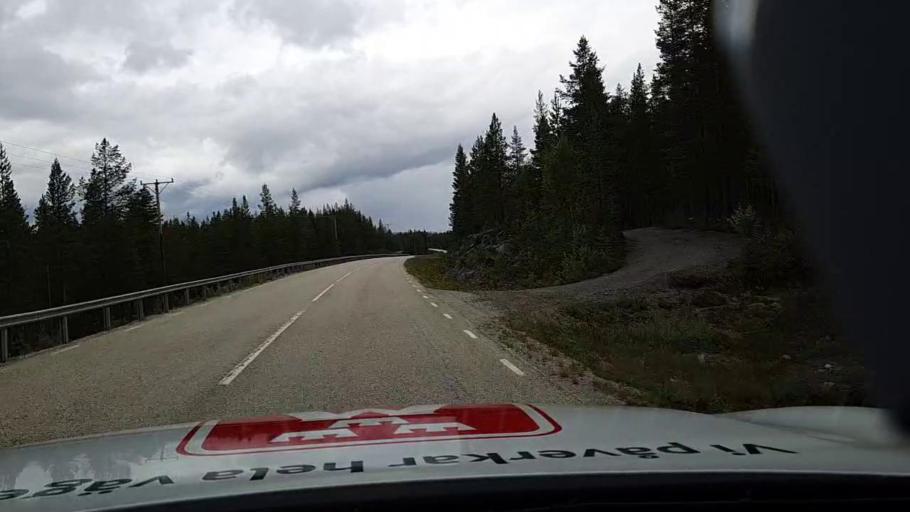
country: SE
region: Jaemtland
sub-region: Are Kommun
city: Jarpen
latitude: 62.7930
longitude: 13.6811
